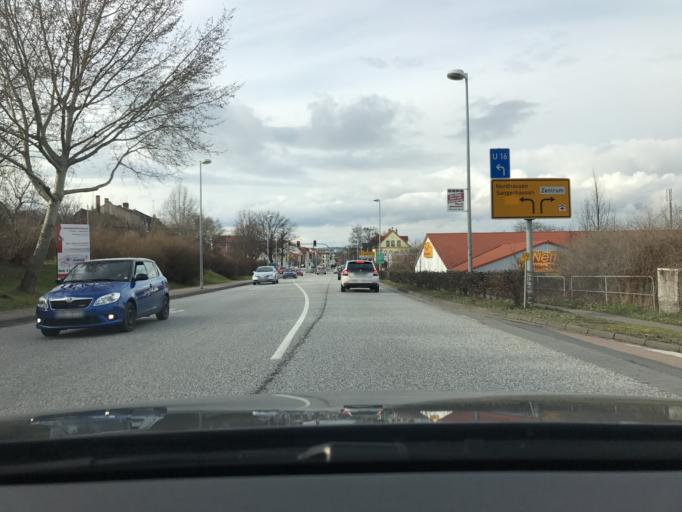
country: DE
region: Saxony-Anhalt
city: Volkstedt
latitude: 51.5206
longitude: 11.5594
